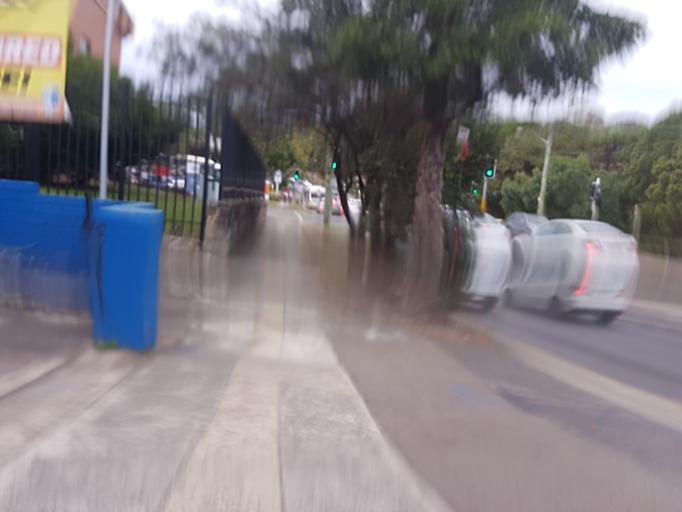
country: AU
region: New South Wales
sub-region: Willoughby
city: Castle Cove
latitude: -33.7862
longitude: 151.2011
